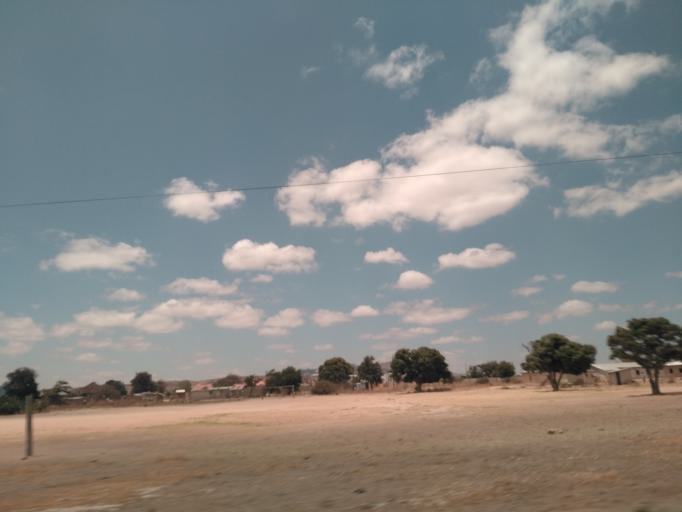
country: TZ
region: Dodoma
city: Kisasa
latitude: -6.1697
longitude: 35.7942
